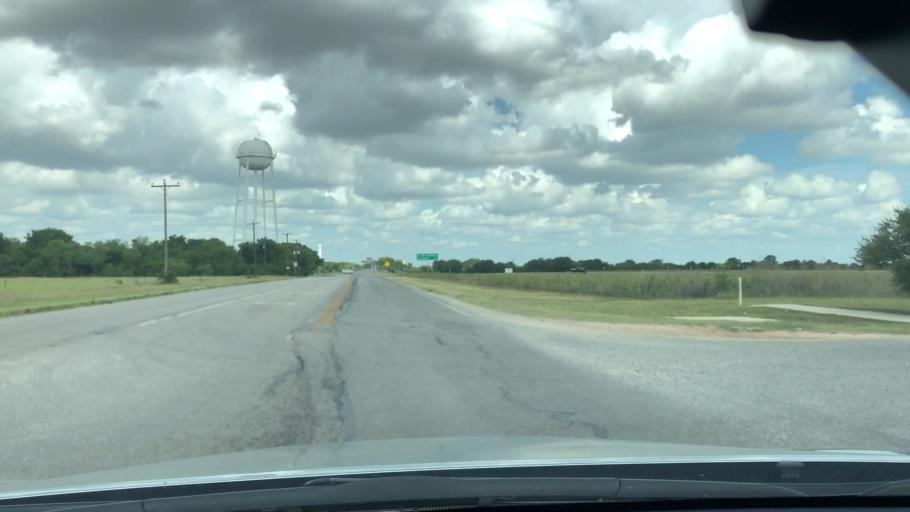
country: US
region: Texas
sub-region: Guadalupe County
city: McQueeney
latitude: 29.5702
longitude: -98.0102
